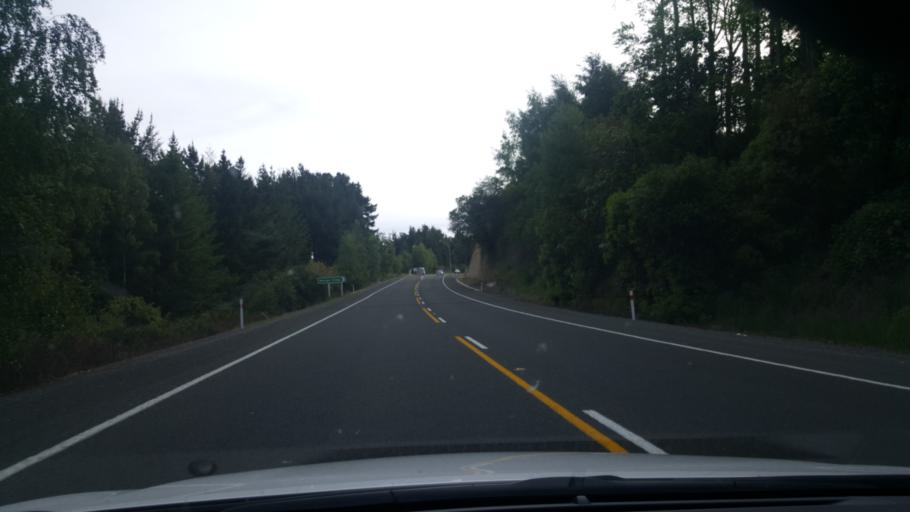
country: NZ
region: Waikato
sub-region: Taupo District
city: Taupo
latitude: -38.6192
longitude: 176.1085
